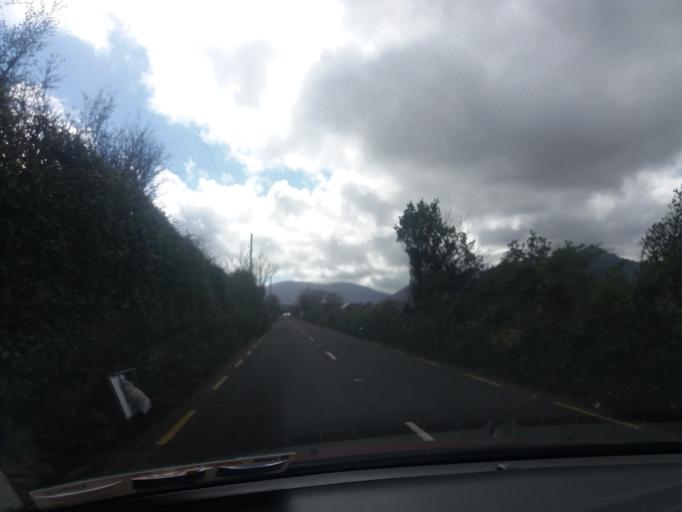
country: IE
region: Munster
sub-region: Ciarrai
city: Dingle
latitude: 52.2243
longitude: -10.1374
